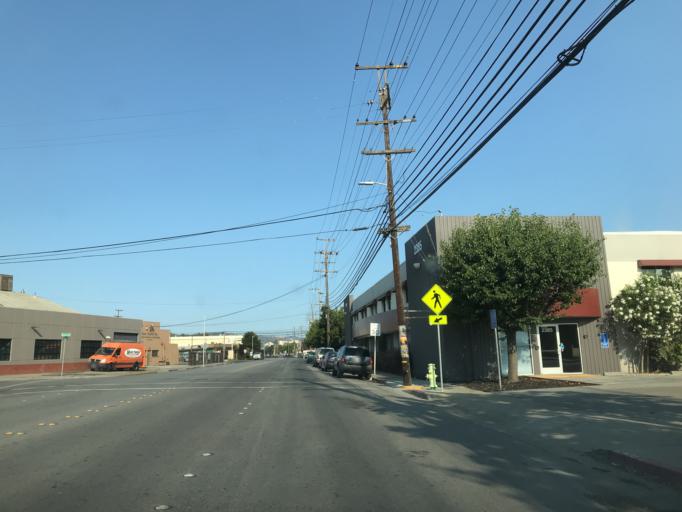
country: US
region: California
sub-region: San Mateo County
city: North Fair Oaks
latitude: 37.4848
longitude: -122.2104
